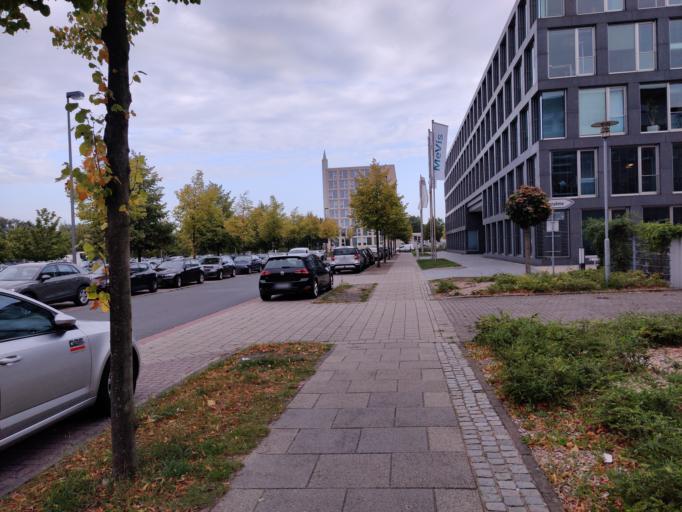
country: DE
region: Bremen
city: Bremen
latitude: 53.1036
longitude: 8.8596
